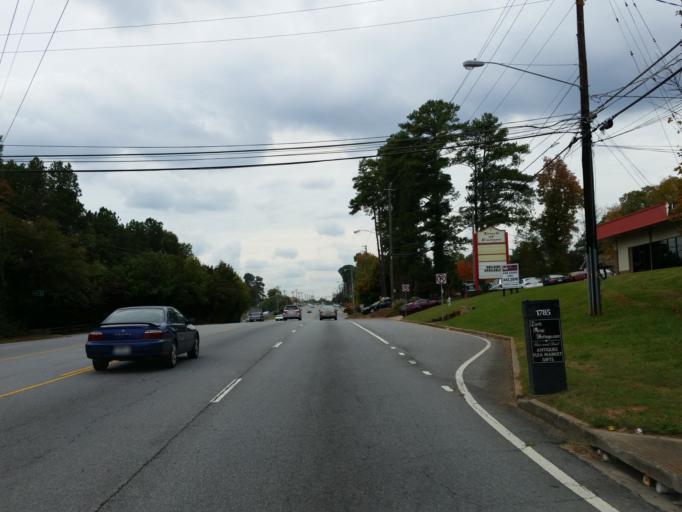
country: US
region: Georgia
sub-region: Cobb County
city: Marietta
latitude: 33.9574
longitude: -84.5007
